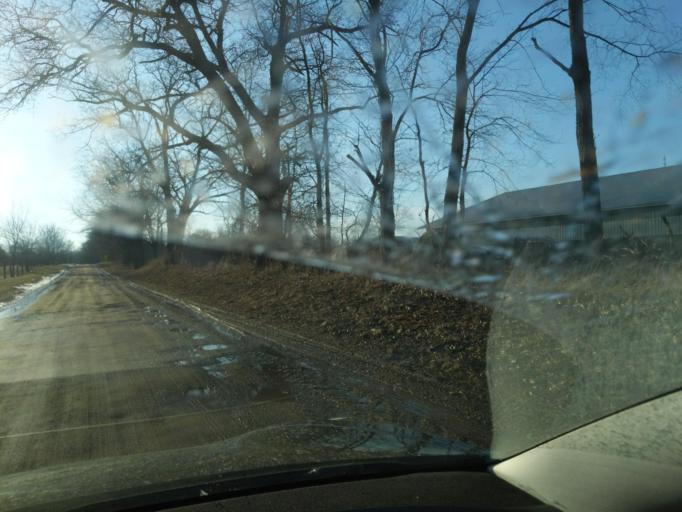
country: US
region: Michigan
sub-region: Ingham County
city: Stockbridge
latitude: 42.5305
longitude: -84.2734
